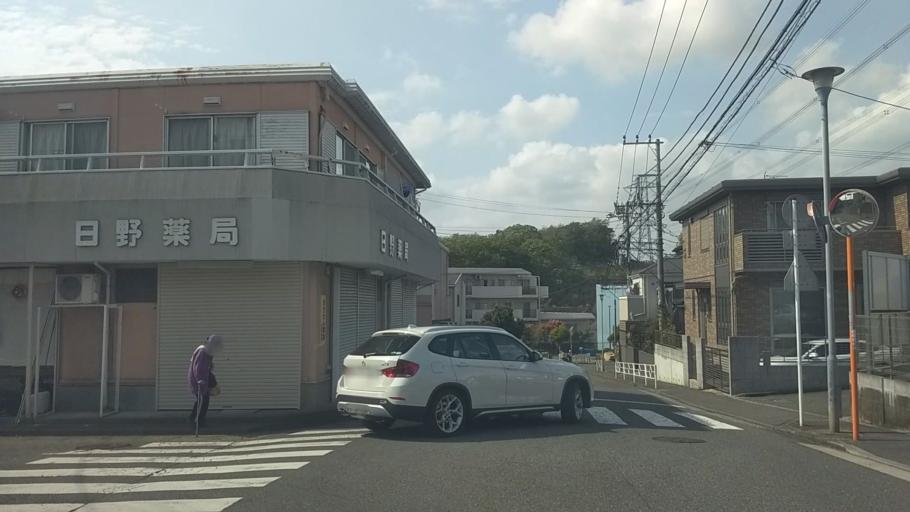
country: JP
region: Kanagawa
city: Kamakura
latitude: 35.3890
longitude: 139.5655
